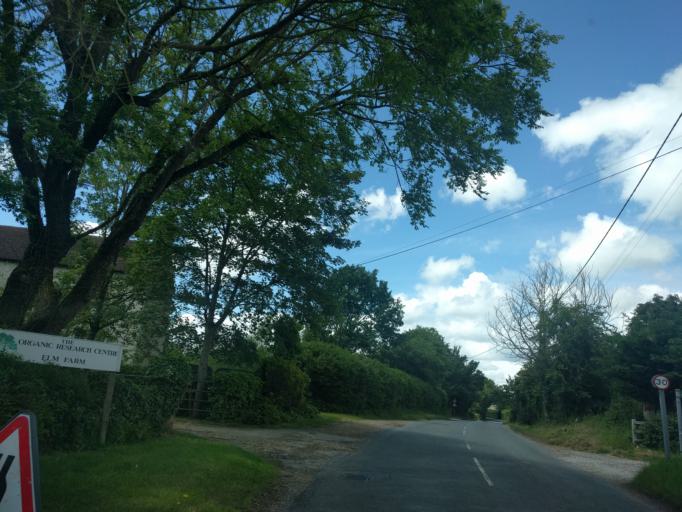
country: GB
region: England
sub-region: West Berkshire
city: Kintbury
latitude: 51.3864
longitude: -1.4067
